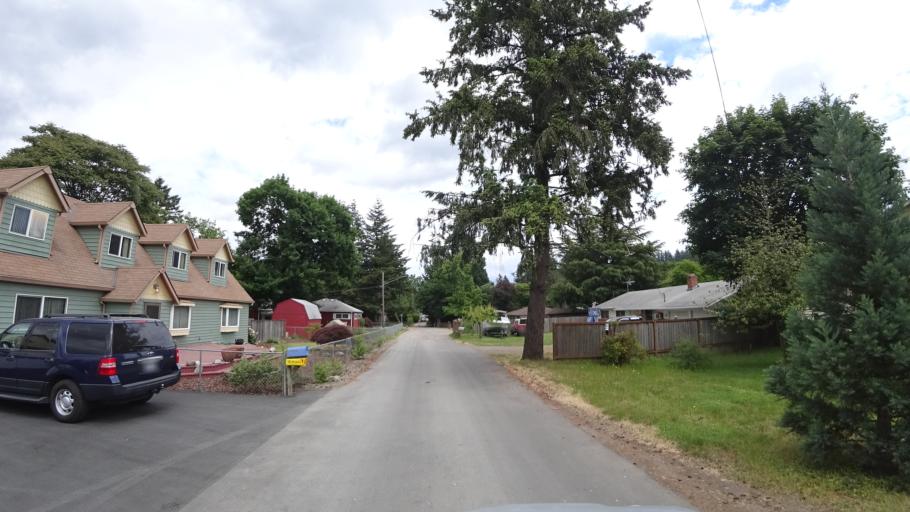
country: US
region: Oregon
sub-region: Clackamas County
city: Happy Valley
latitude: 45.4960
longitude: -122.5174
